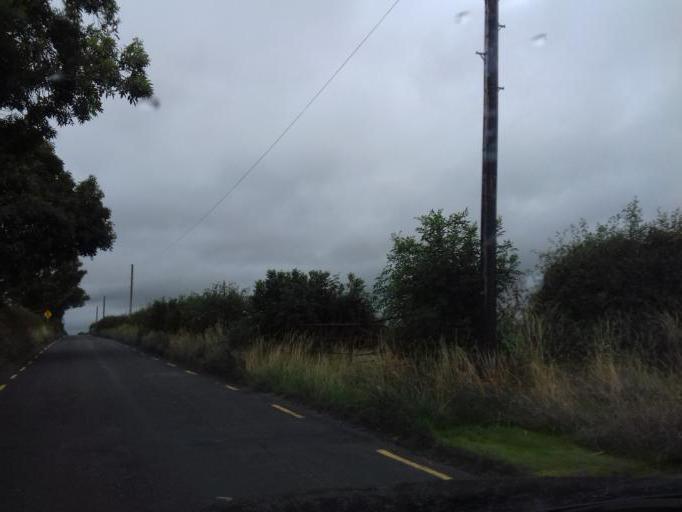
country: IE
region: Leinster
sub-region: Kilkenny
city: Graiguenamanagh
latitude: 52.6120
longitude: -7.0312
